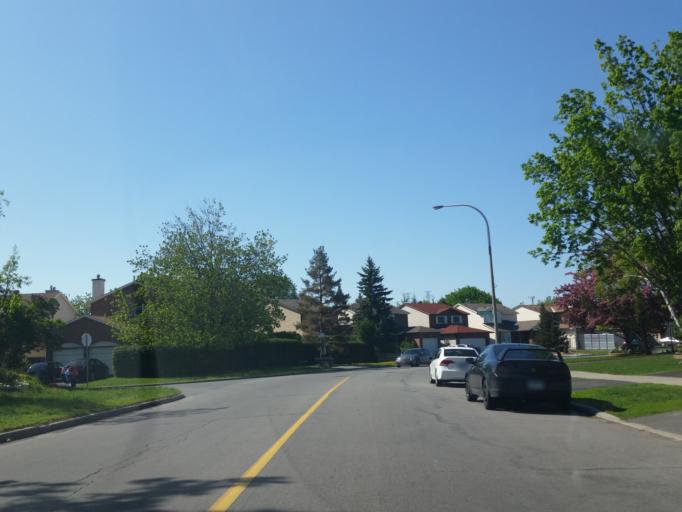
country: CA
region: Ontario
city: Ottawa
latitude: 45.3526
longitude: -75.7090
